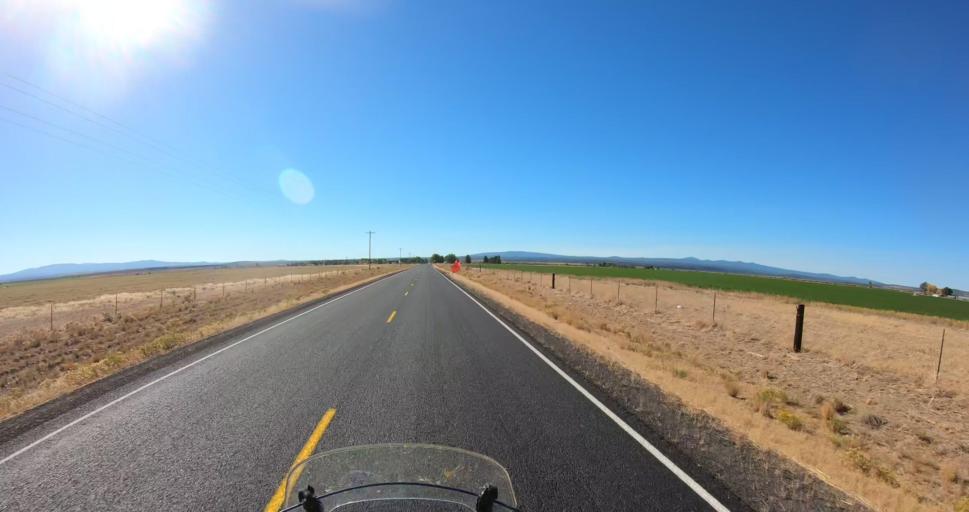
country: US
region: Oregon
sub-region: Deschutes County
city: La Pine
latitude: 43.1277
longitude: -121.0281
